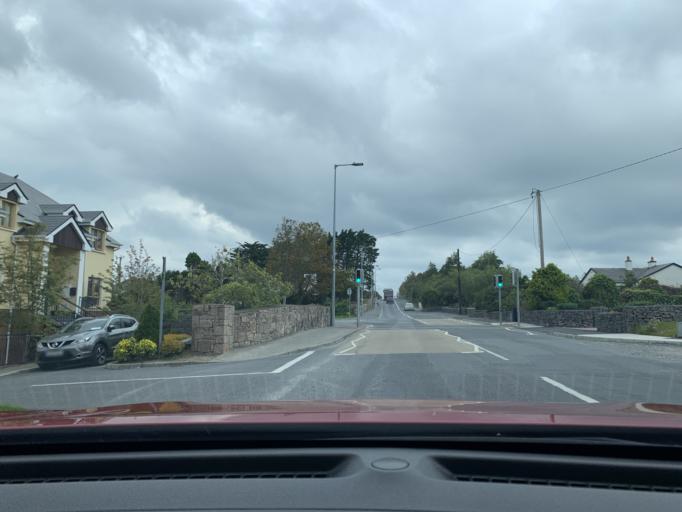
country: IE
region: Connaught
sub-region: County Galway
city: Bearna
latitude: 53.2696
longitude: -9.1176
